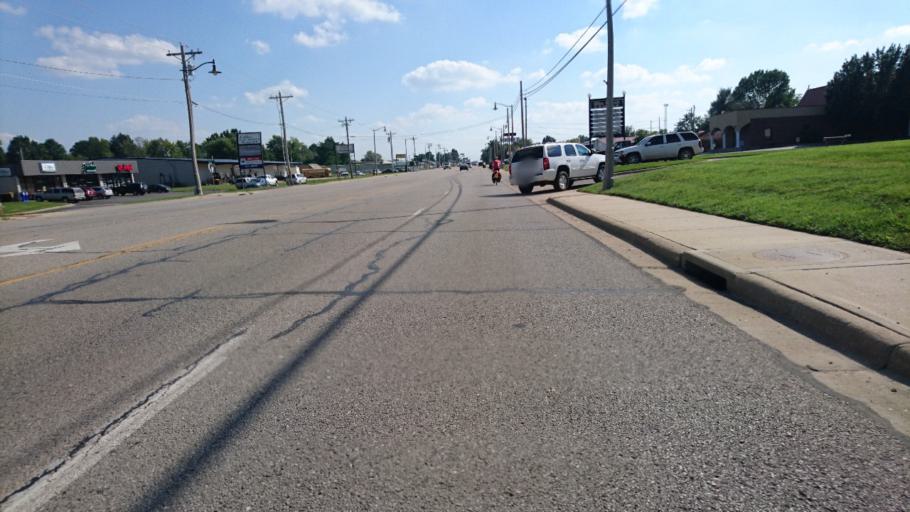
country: US
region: Missouri
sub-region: Laclede County
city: Lebanon
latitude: 37.6606
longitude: -92.6677
